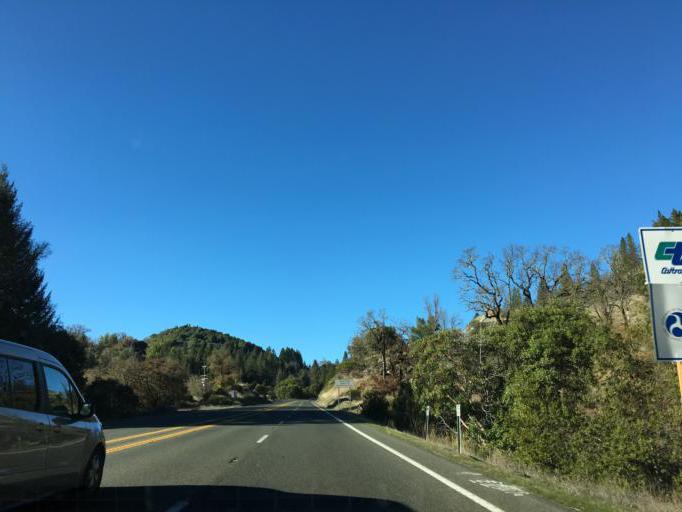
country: US
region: California
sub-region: Mendocino County
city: Laytonville
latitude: 39.6164
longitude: -123.4610
